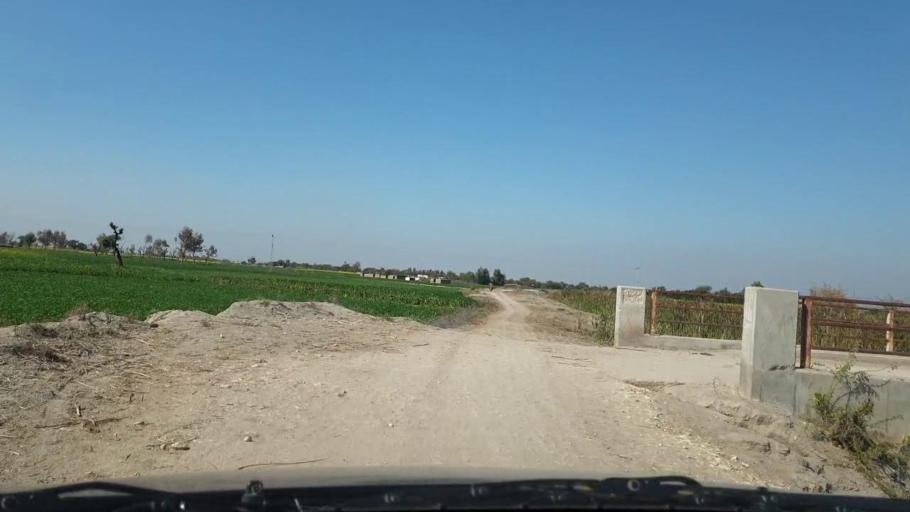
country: PK
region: Sindh
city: Khadro
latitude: 26.1477
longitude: 68.7717
